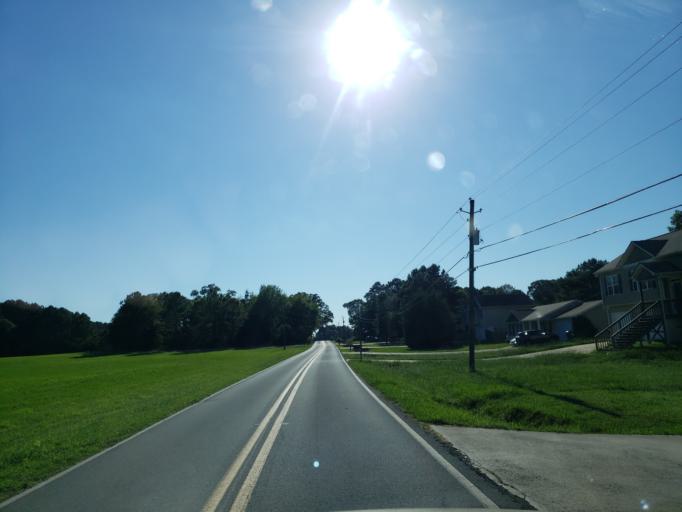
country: US
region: Georgia
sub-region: Bartow County
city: Euharlee
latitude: 34.1086
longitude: -84.9192
